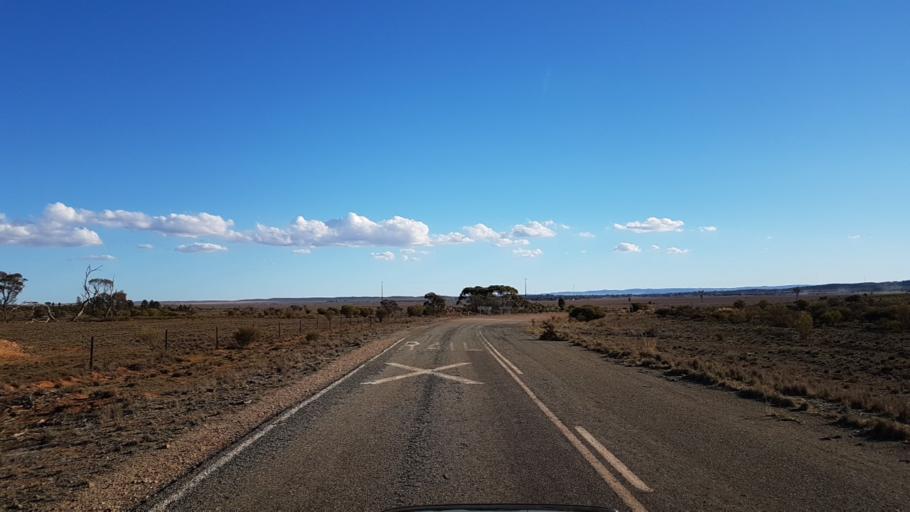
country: AU
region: South Australia
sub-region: Peterborough
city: Peterborough
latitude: -32.9595
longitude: 138.8939
